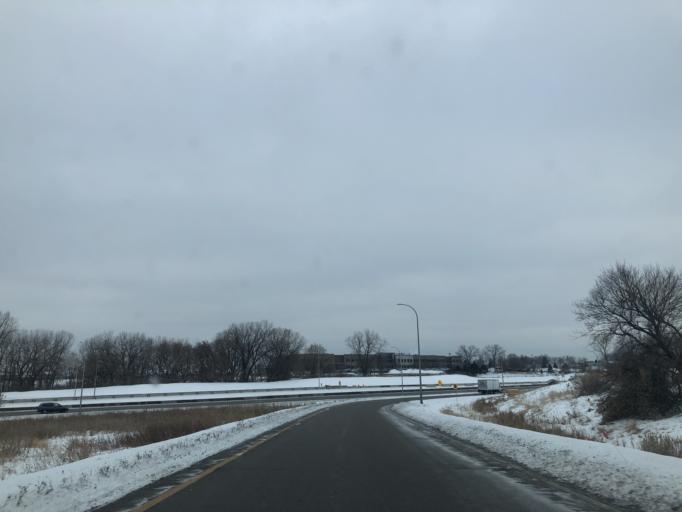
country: US
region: Minnesota
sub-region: Ramsey County
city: New Brighton
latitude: 45.0684
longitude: -93.1842
